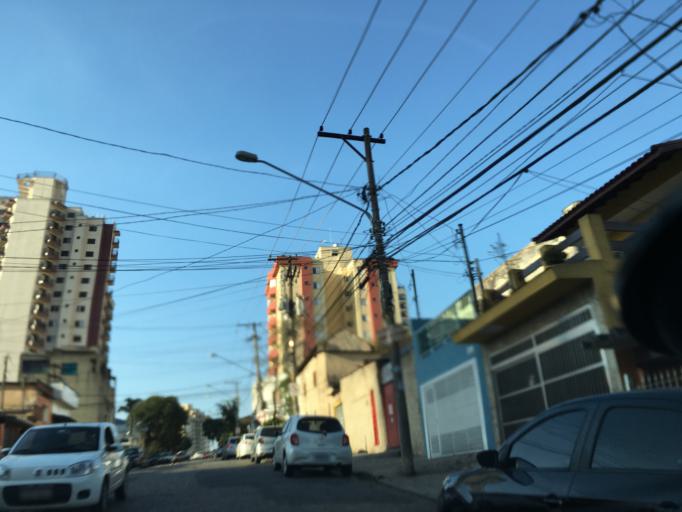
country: BR
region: Sao Paulo
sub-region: Sao Paulo
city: Sao Paulo
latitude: -23.4919
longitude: -46.6369
